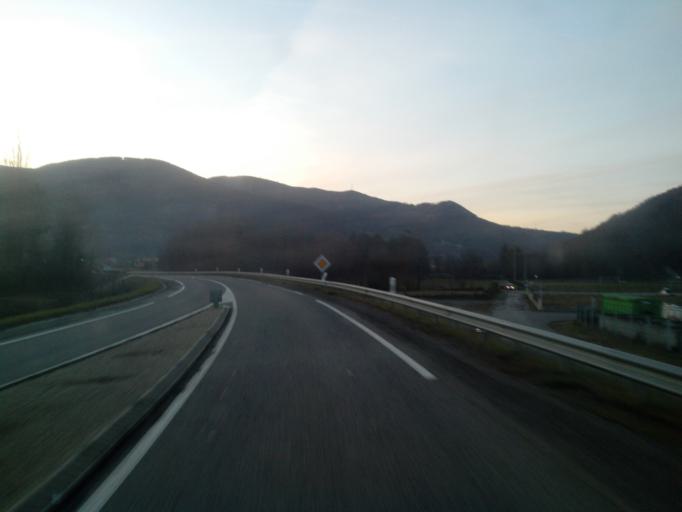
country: FR
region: Midi-Pyrenees
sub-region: Departement de l'Ariege
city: Saint-Paul-de-Jarrat
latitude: 42.9181
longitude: 1.6552
